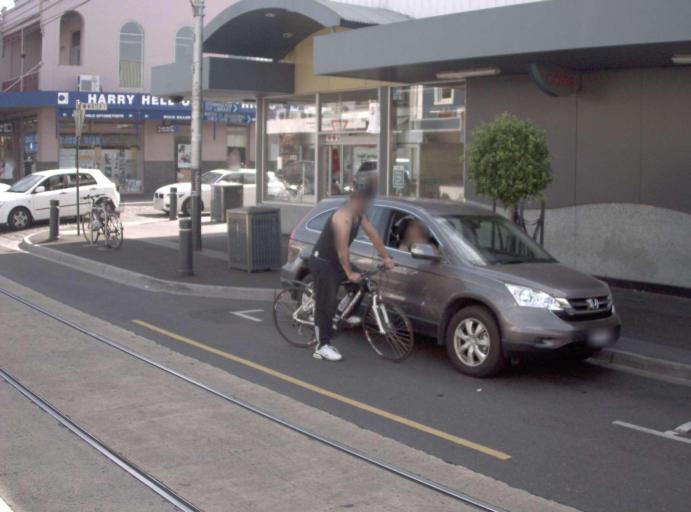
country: AU
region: Victoria
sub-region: Glen Eira
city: Caulfield North
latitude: -37.8603
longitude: 145.0287
